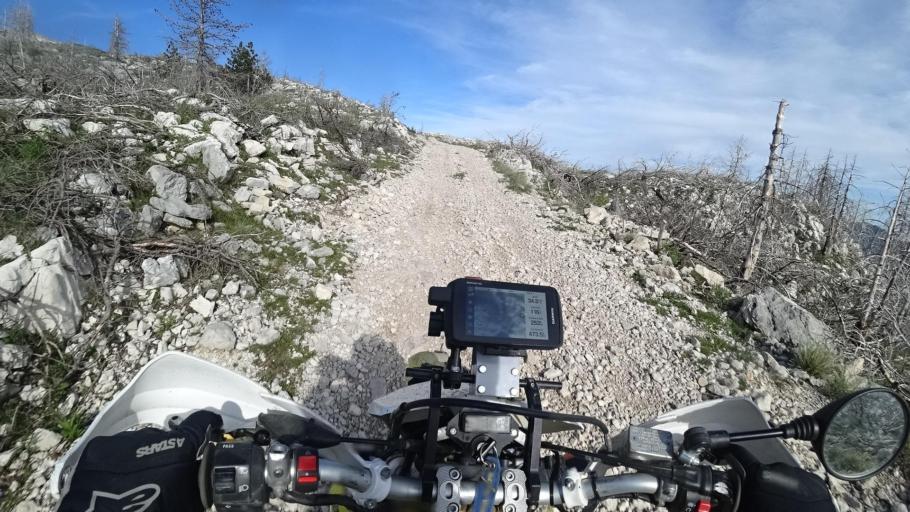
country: BA
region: Federation of Bosnia and Herzegovina
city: Kocerin
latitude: 43.5781
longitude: 17.5394
